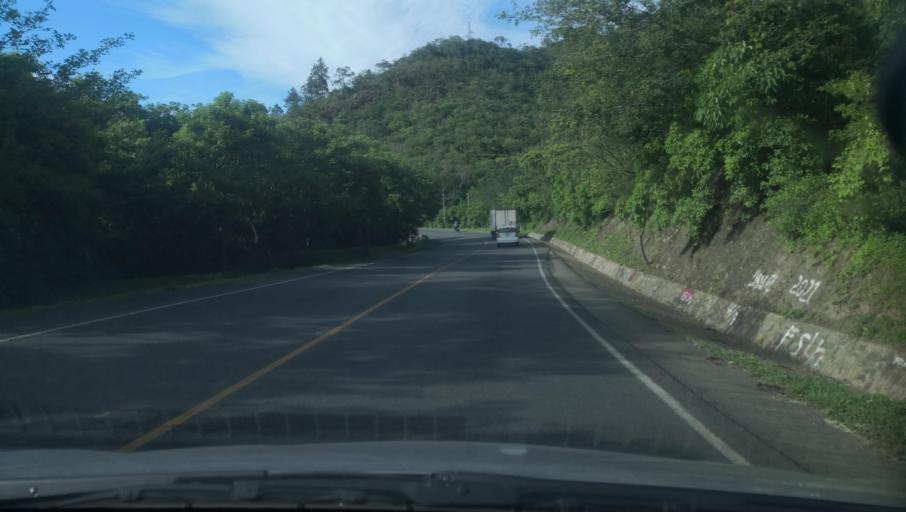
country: NI
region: Madriz
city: Totogalpa
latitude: 13.5680
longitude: -86.4839
